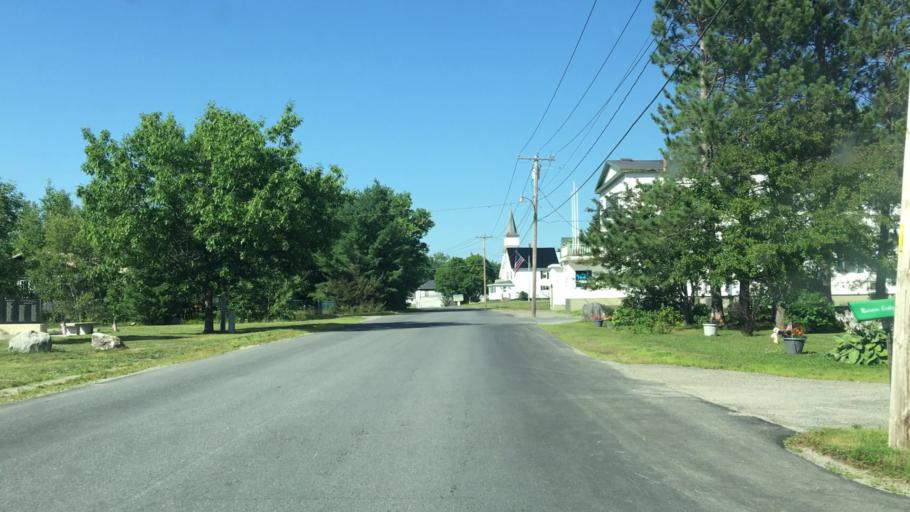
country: US
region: Maine
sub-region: Penobscot County
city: Howland
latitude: 45.2431
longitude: -68.6463
